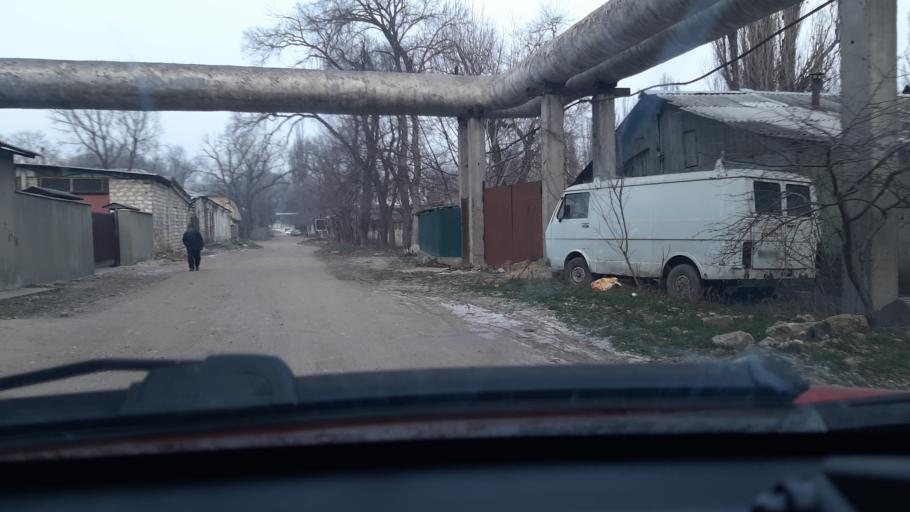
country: MD
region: Chisinau
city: Chisinau
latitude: 46.9890
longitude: 28.8889
